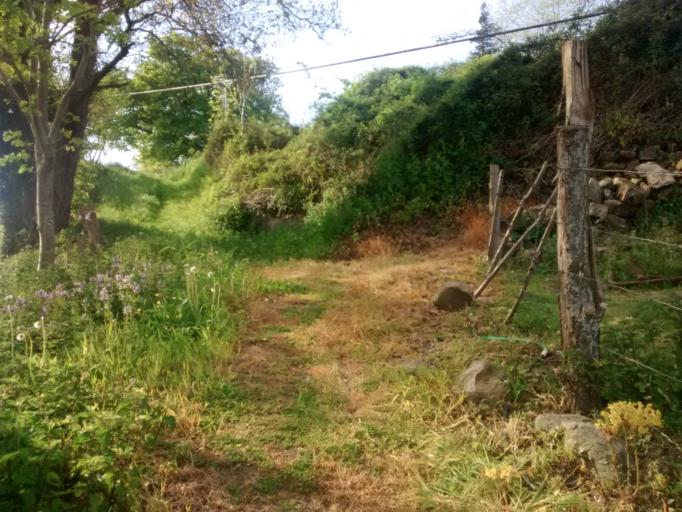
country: ES
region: Cantabria
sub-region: Provincia de Cantabria
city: Entrambasaguas
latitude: 43.3391
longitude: -3.6657
